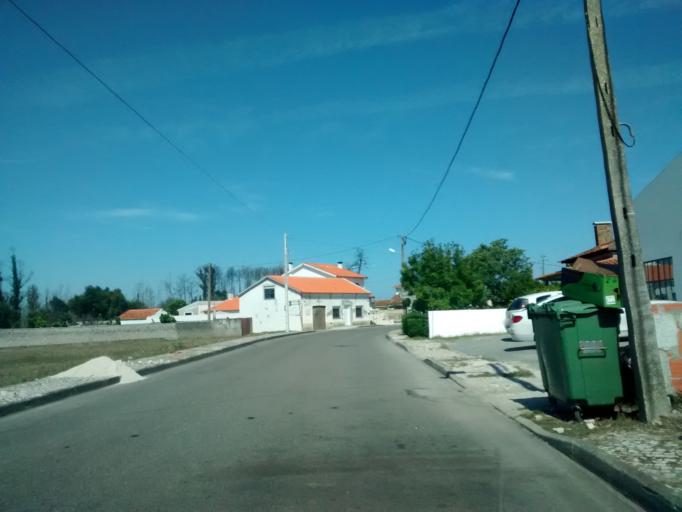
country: PT
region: Coimbra
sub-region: Mira
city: Mira
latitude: 40.4339
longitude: -8.7119
